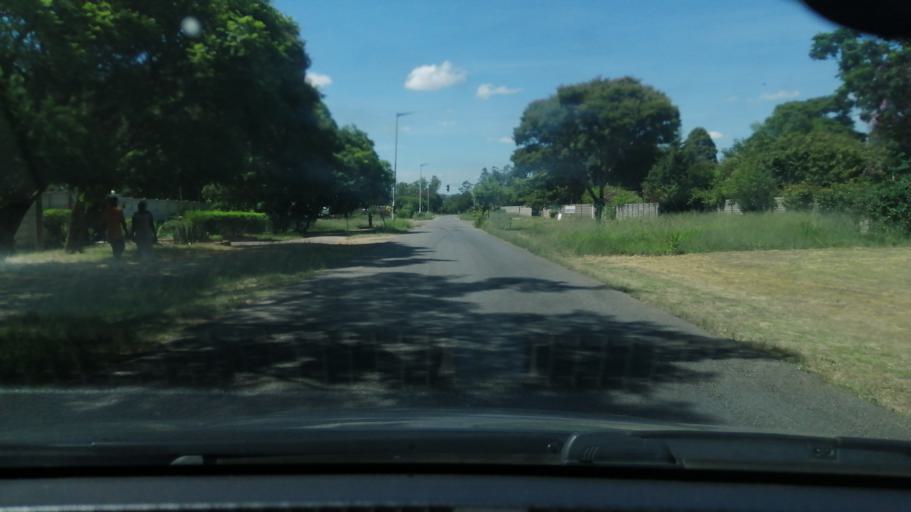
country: ZW
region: Harare
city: Epworth
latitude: -17.8286
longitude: 31.1250
